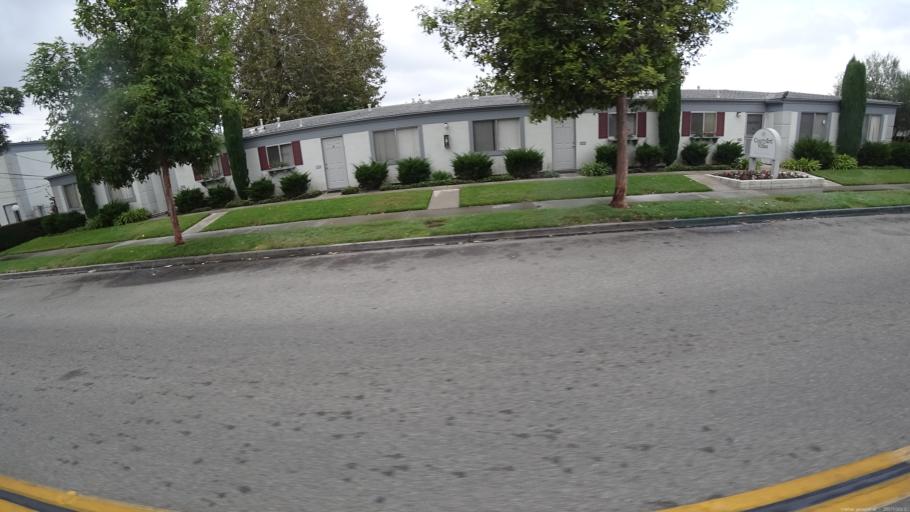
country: US
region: California
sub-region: Orange County
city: Garden Grove
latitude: 33.7600
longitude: -117.9621
